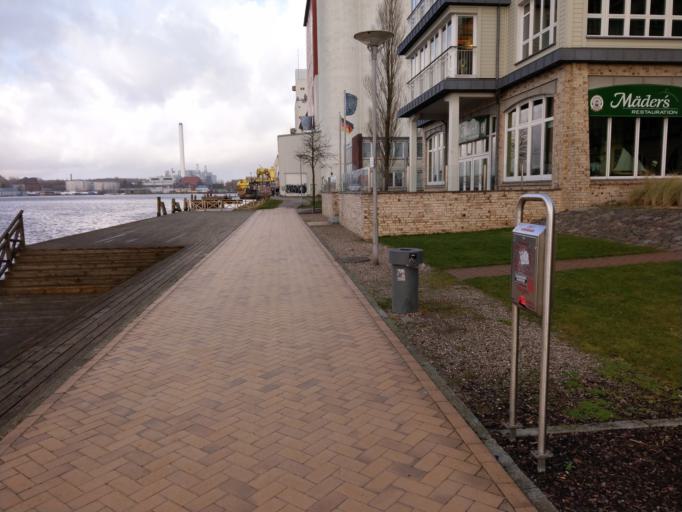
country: DE
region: Schleswig-Holstein
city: Flensburg
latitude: 54.7951
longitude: 9.4373
